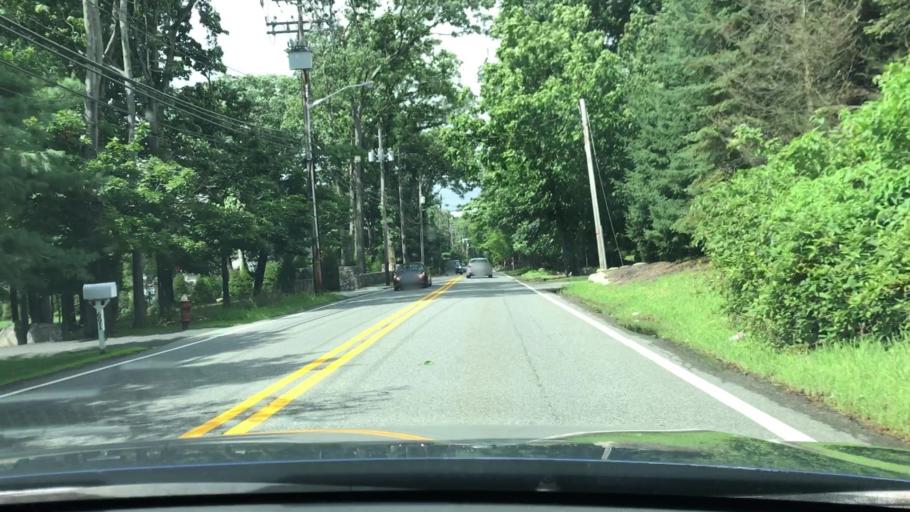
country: US
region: New Jersey
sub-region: Bergen County
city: Wyckoff
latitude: 41.0339
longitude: -74.1671
